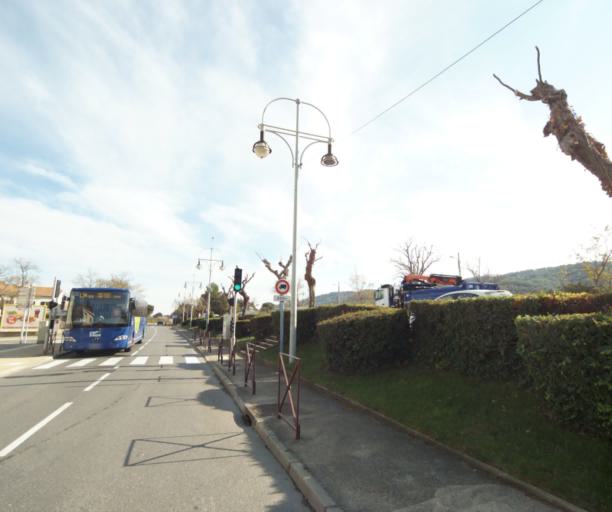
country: FR
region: Provence-Alpes-Cote d'Azur
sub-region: Departement des Bouches-du-Rhone
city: Chateauneuf-les-Martigues
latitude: 43.3975
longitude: 5.1122
